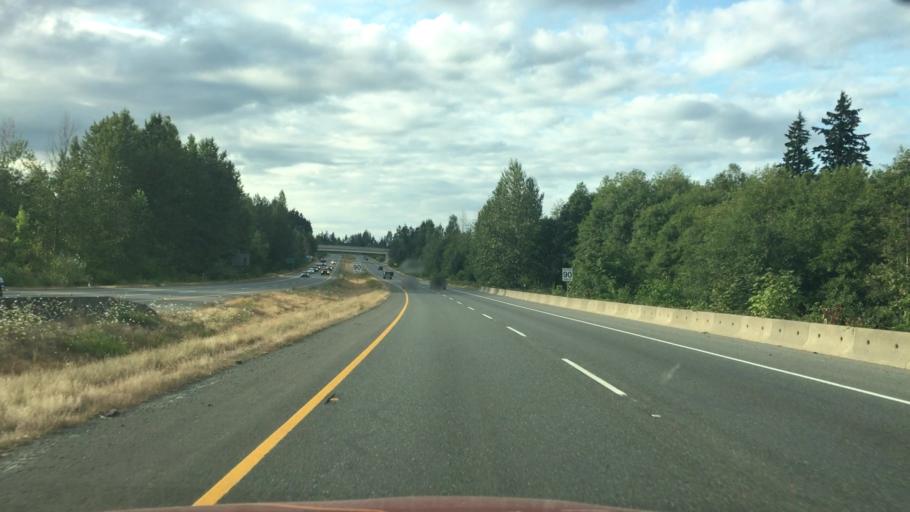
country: CA
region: British Columbia
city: Nanaimo
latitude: 49.1750
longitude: -123.9833
